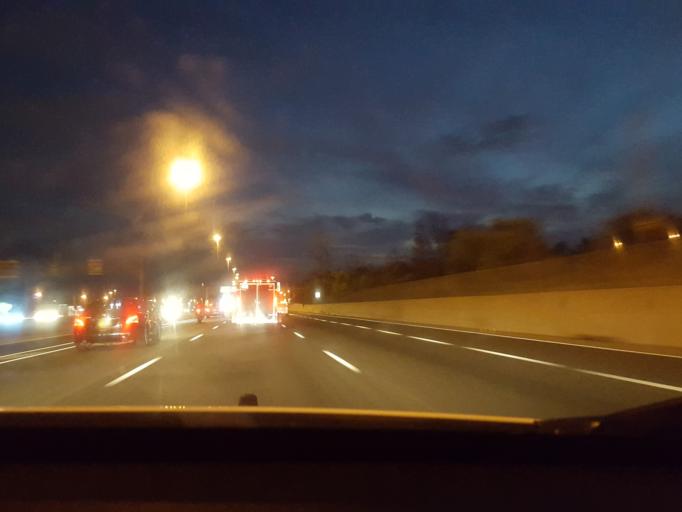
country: CA
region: Ontario
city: Oakville
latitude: 43.4181
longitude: -79.7319
